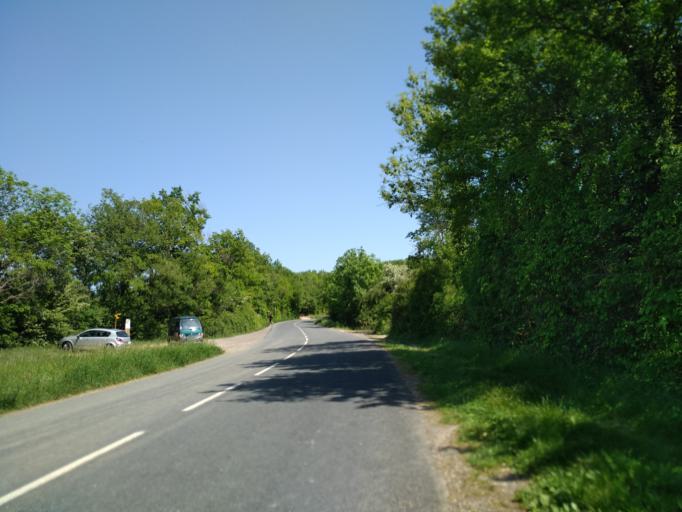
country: FR
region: Rhone-Alpes
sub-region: Departement du Rhone
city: Fontaines-sur-Saone
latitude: 45.8280
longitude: 4.8123
